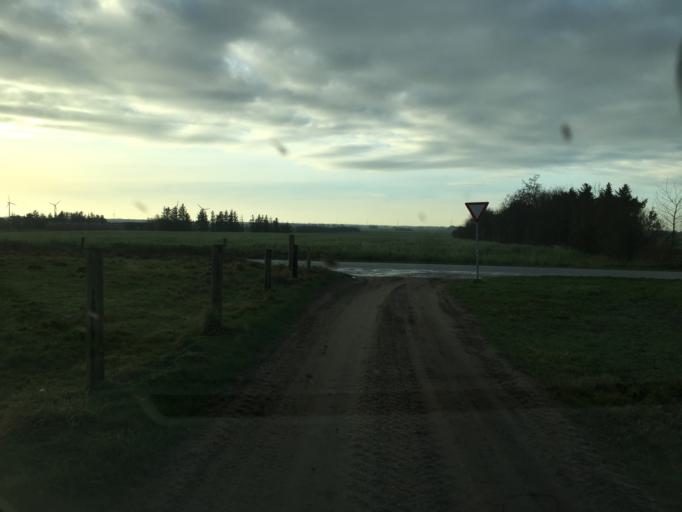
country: DK
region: South Denmark
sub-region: Tonder Kommune
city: Logumkloster
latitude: 55.1108
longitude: 8.8641
